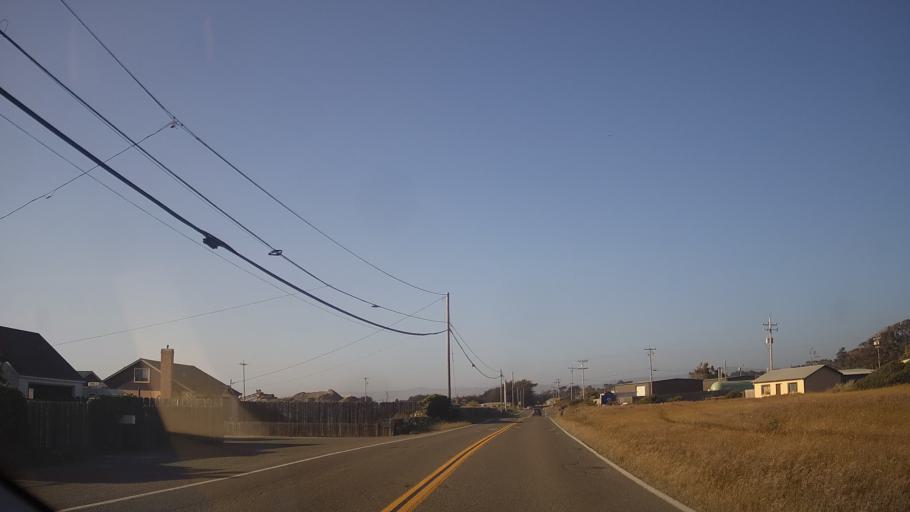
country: US
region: California
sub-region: Mendocino County
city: Fort Bragg
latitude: 39.4652
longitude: -123.8050
